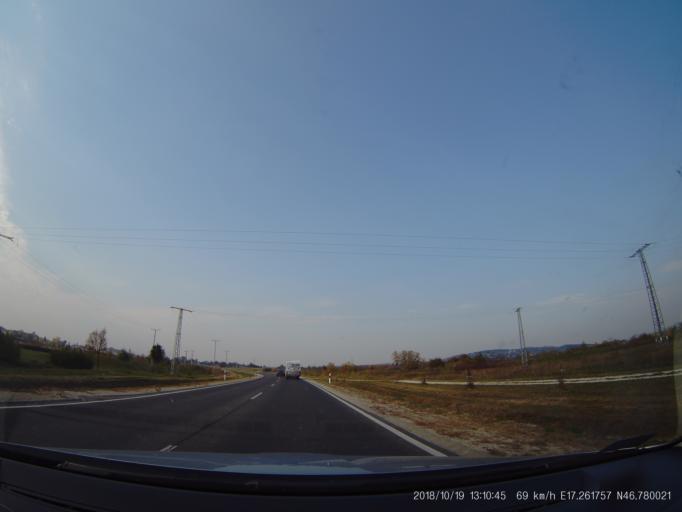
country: HU
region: Zala
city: Keszthely
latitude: 46.7800
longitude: 17.2617
